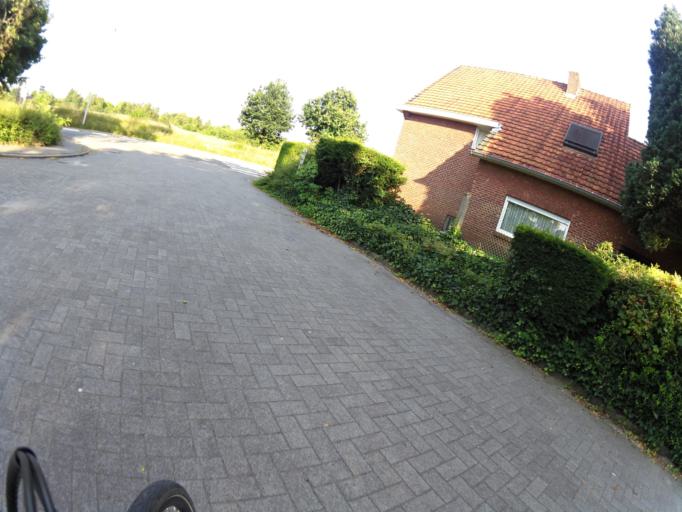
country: BE
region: Flanders
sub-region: Provincie Limburg
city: Lommel
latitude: 51.2203
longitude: 5.3098
